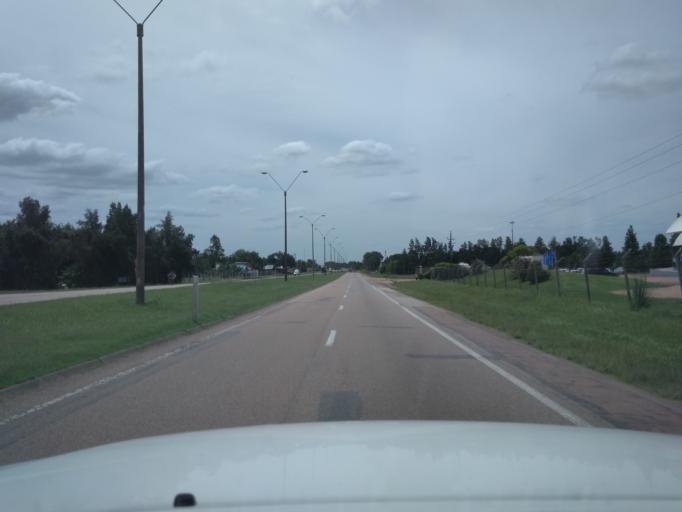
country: UY
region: Canelones
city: Joanico
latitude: -34.5988
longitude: -56.2618
